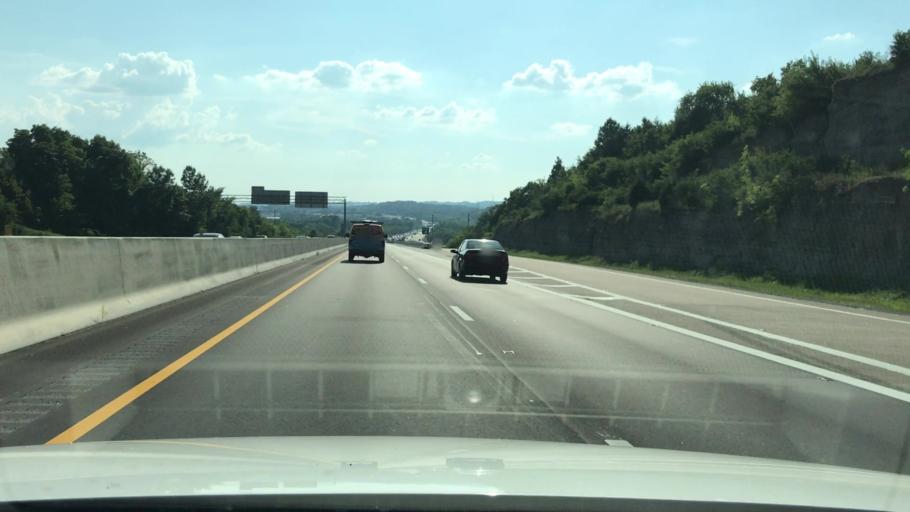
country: US
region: Tennessee
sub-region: Sumner County
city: Hendersonville
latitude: 36.3132
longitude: -86.6595
